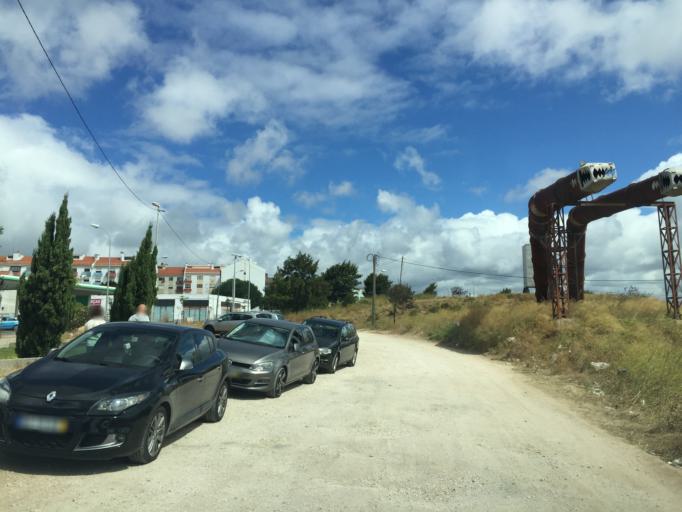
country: PT
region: Lisbon
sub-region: Odivelas
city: Famoes
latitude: 38.7763
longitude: -9.2295
